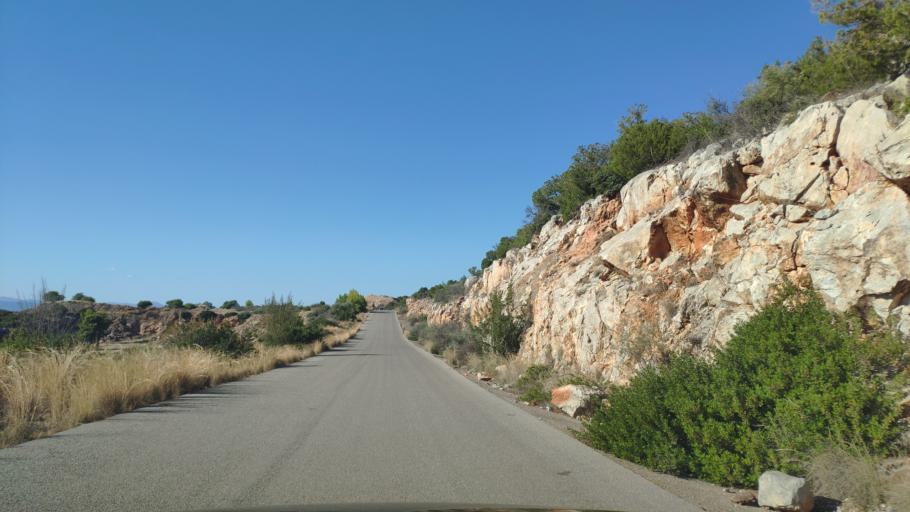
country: GR
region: Attica
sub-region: Nomos Piraios
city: Galatas
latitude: 37.5652
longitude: 23.3621
